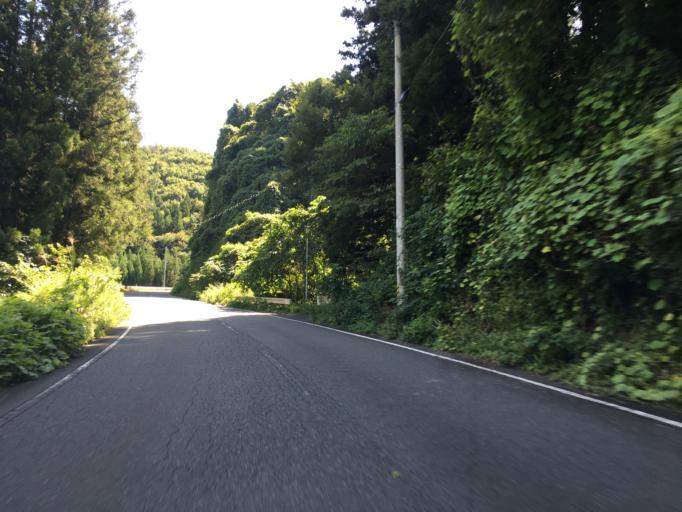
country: JP
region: Fukushima
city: Sukagawa
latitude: 37.2939
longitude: 140.4880
